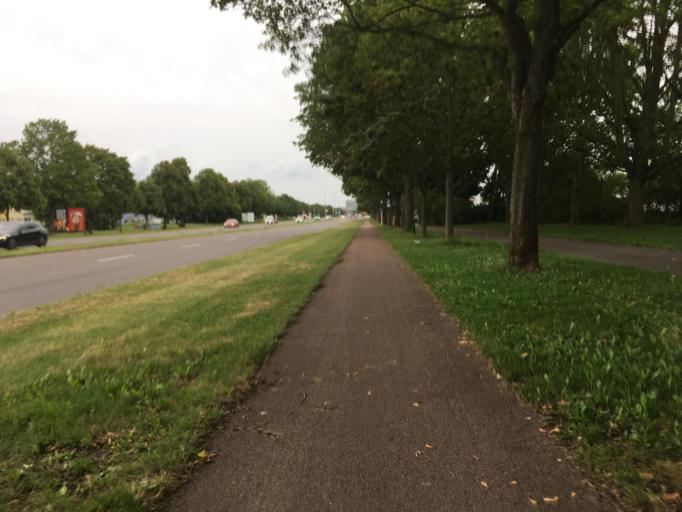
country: DE
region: Brandenburg
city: Schwedt (Oder)
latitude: 53.0663
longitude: 14.2644
